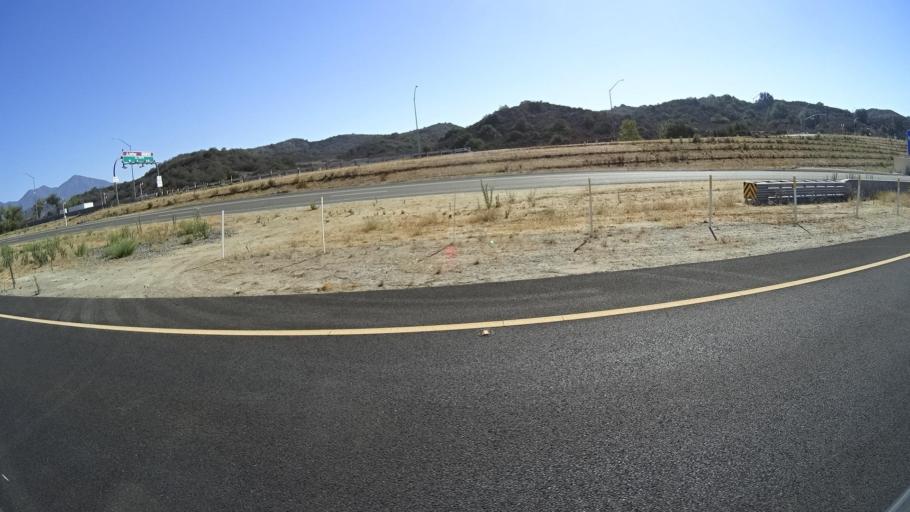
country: US
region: California
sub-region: Orange County
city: Las Flores
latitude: 33.5890
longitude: -117.6105
